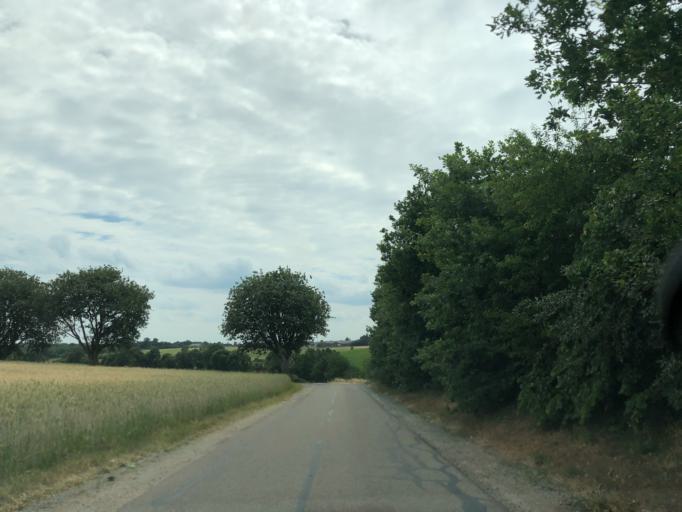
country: DK
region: Central Jutland
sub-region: Silkeborg Kommune
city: Svejbaek
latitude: 56.2027
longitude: 9.6901
